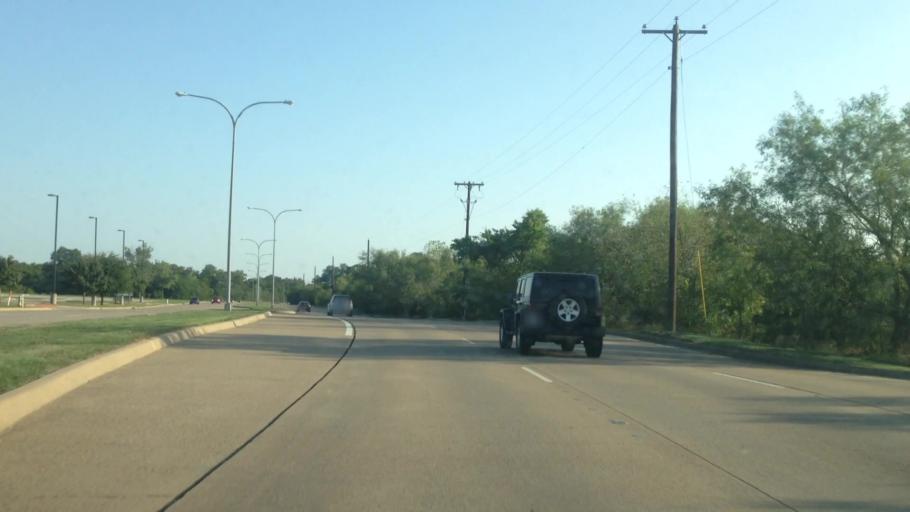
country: US
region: Texas
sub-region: Tarrant County
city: Pantego
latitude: 32.7458
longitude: -97.1733
